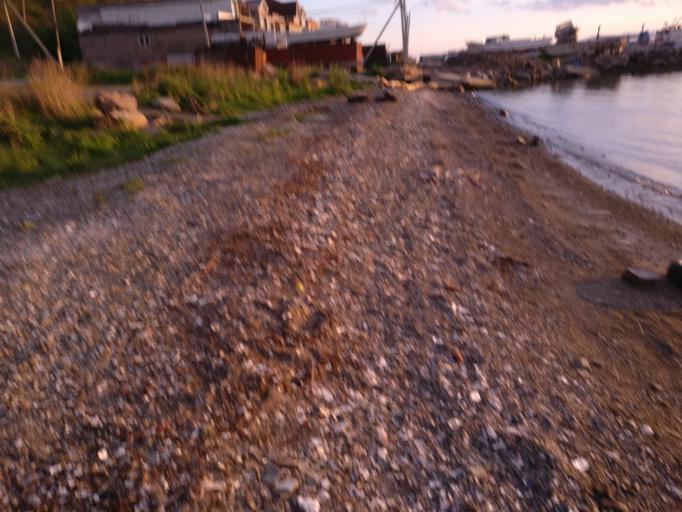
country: RU
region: Primorskiy
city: Vladivostok
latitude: 43.1805
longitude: 131.9075
